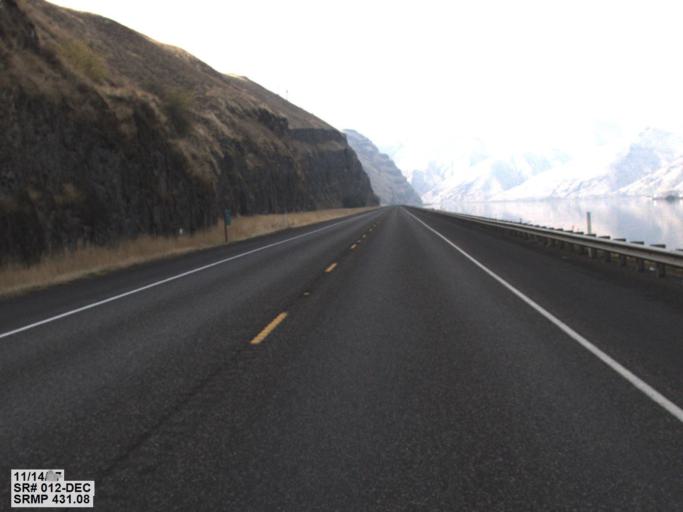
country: US
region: Washington
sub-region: Asotin County
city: Clarkston Heights-Vineland
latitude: 46.4160
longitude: -117.0986
